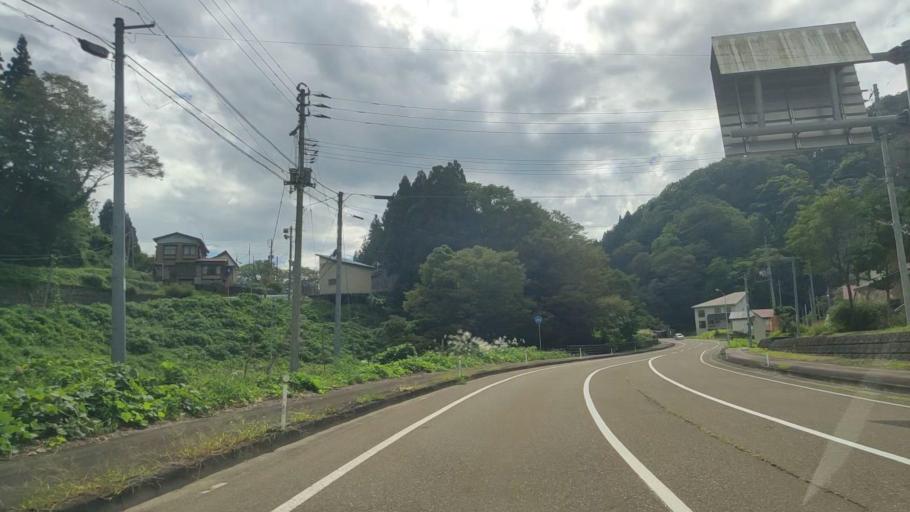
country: JP
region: Niigata
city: Arai
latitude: 36.9542
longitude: 138.2773
